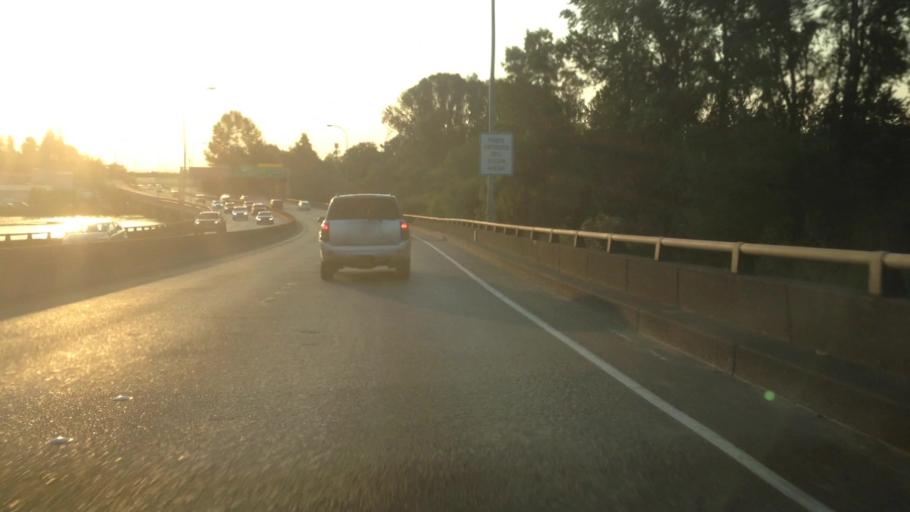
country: US
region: Washington
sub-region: King County
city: Seattle
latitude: 47.6435
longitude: -122.3112
